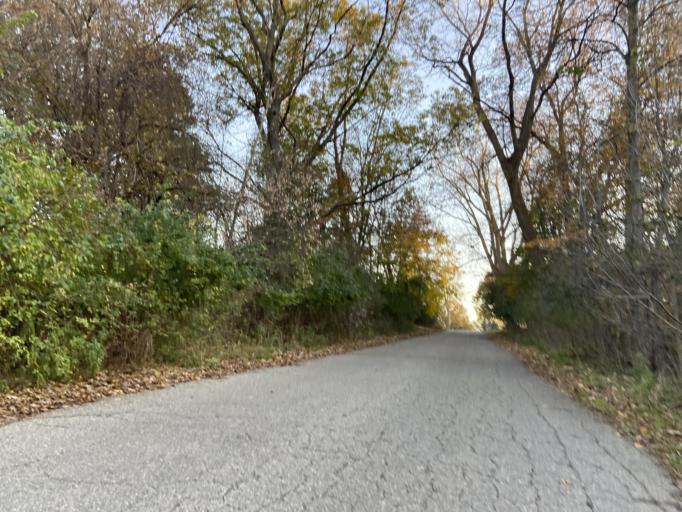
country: US
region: Michigan
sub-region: Oakland County
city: Franklin
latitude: 42.5340
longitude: -83.3321
